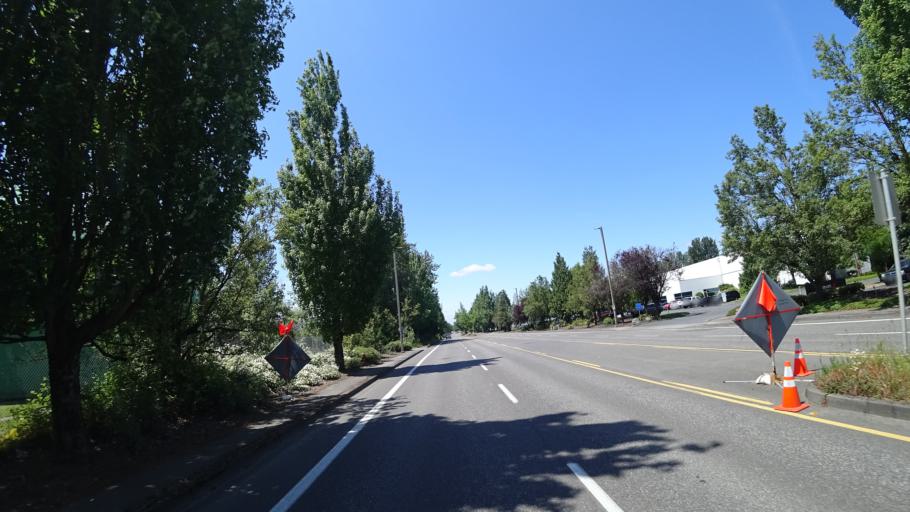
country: US
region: Oregon
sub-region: Multnomah County
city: Fairview
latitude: 45.5564
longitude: -122.4951
